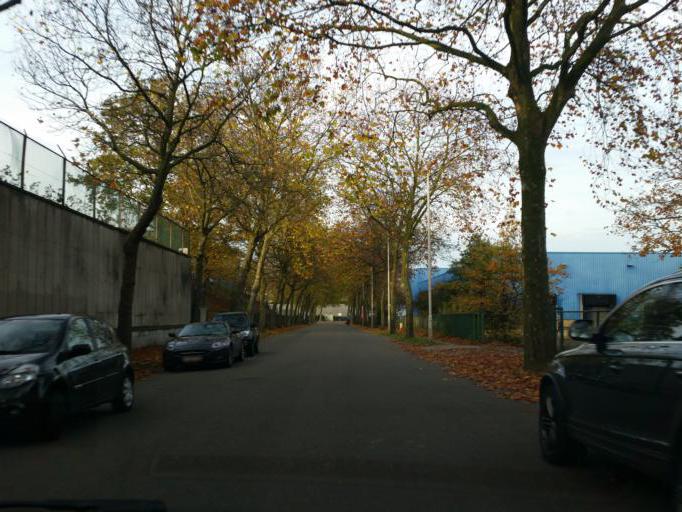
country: BE
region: Flanders
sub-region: Provincie Antwerpen
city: Hoboken
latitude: 51.1770
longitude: 4.3381
